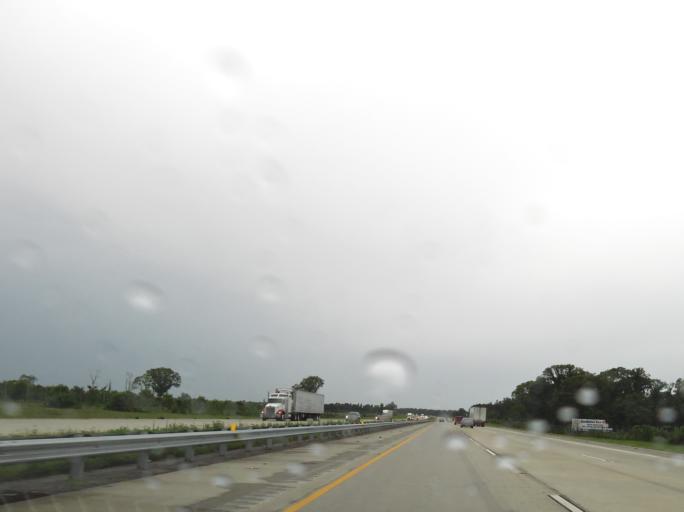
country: US
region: Georgia
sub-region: Dooly County
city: Vienna
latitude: 32.0445
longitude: -83.7640
